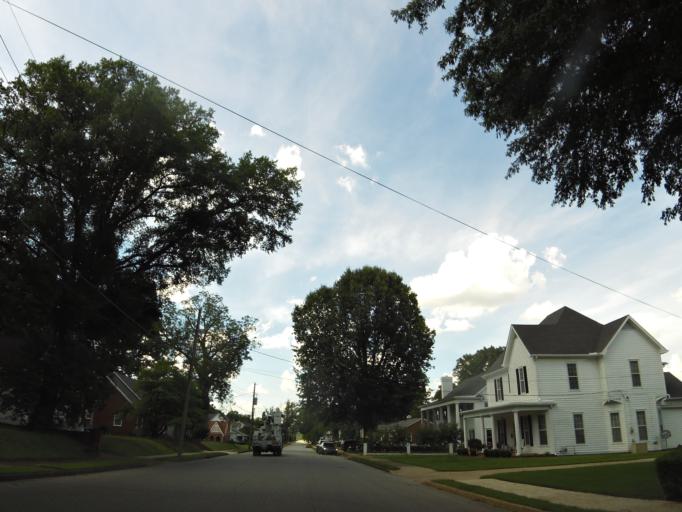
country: US
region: Tennessee
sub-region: Gibson County
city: Trenton
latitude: 35.9727
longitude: -88.9432
